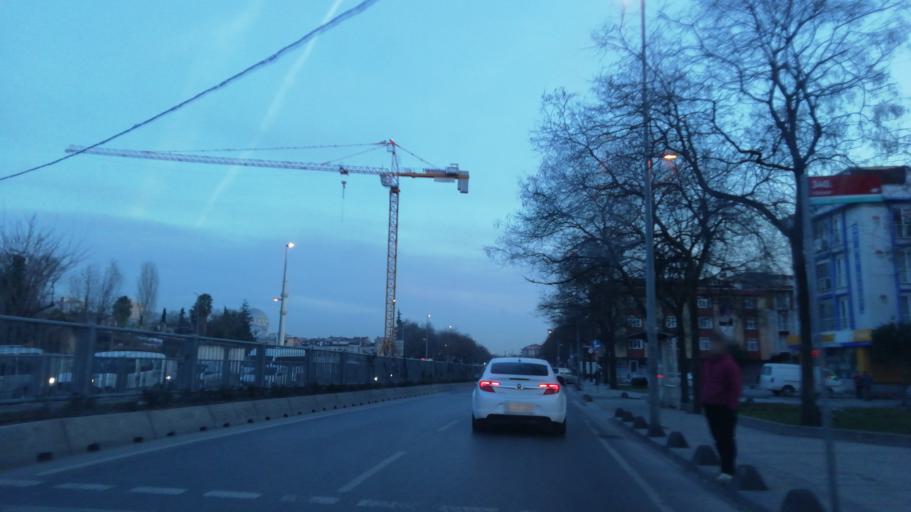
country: TR
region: Istanbul
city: Bagcilar
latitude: 41.0274
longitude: 28.8471
